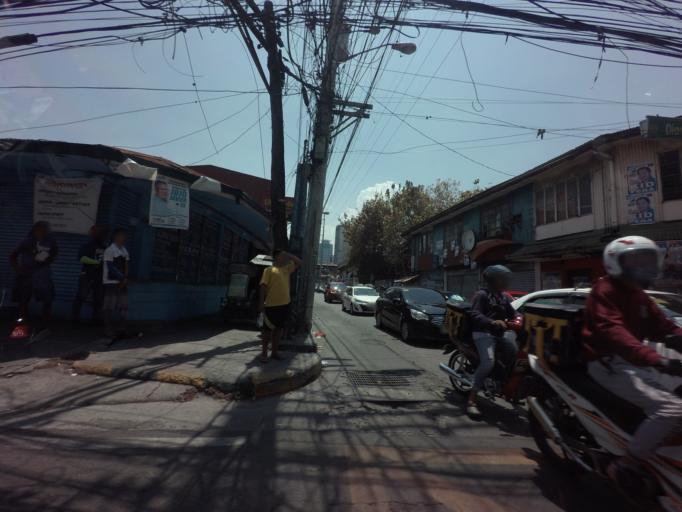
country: PH
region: Metro Manila
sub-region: Makati City
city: Makati City
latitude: 14.5568
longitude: 121.0038
